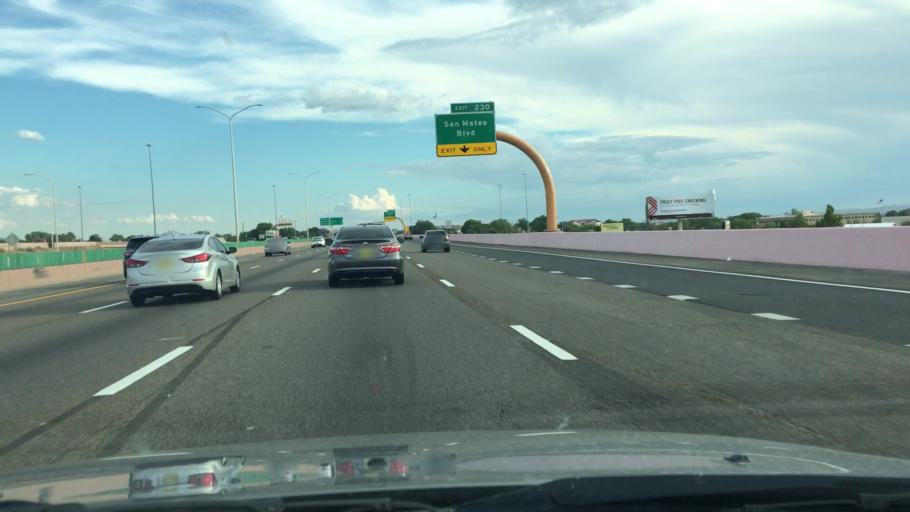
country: US
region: New Mexico
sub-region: Bernalillo County
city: North Valley
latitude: 35.1600
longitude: -106.5873
